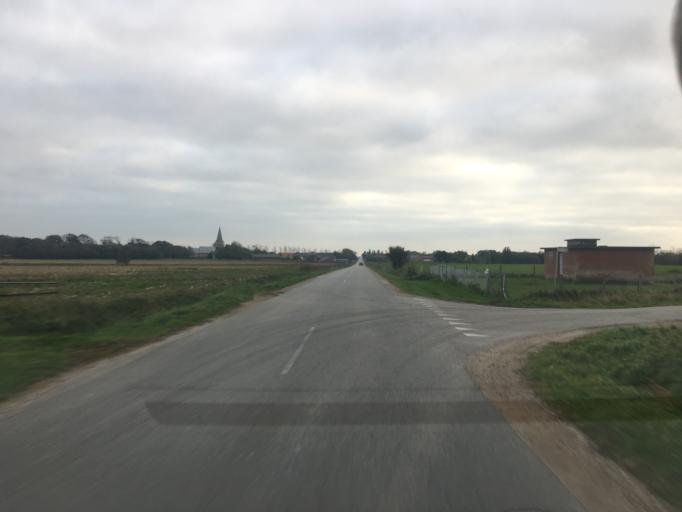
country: DE
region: Schleswig-Holstein
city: Aventoft
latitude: 54.9751
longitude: 8.7466
